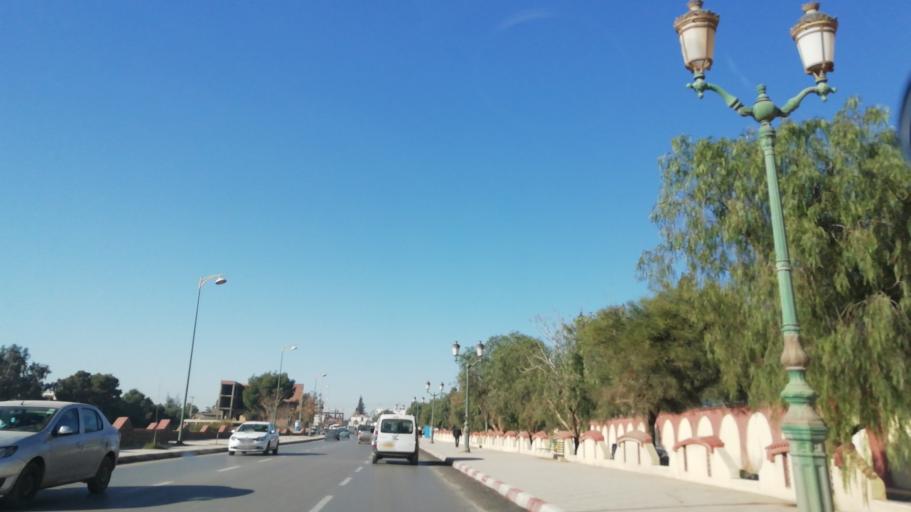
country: DZ
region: Tlemcen
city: Nedroma
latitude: 34.8463
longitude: -1.7370
